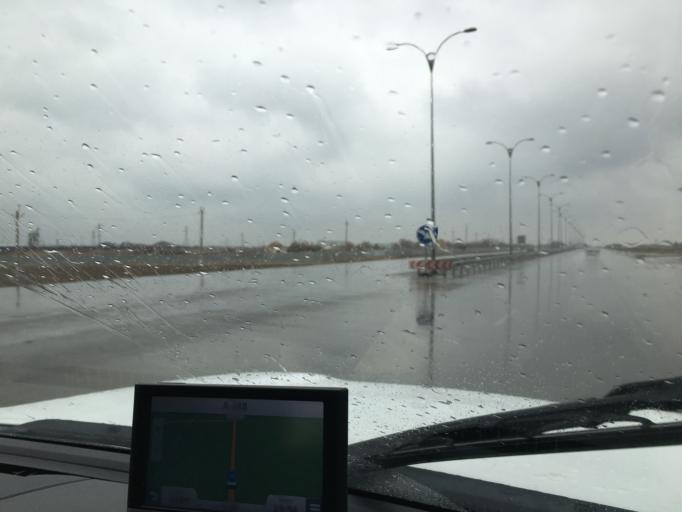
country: TM
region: Mary
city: Mary
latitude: 37.5415
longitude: 61.8765
